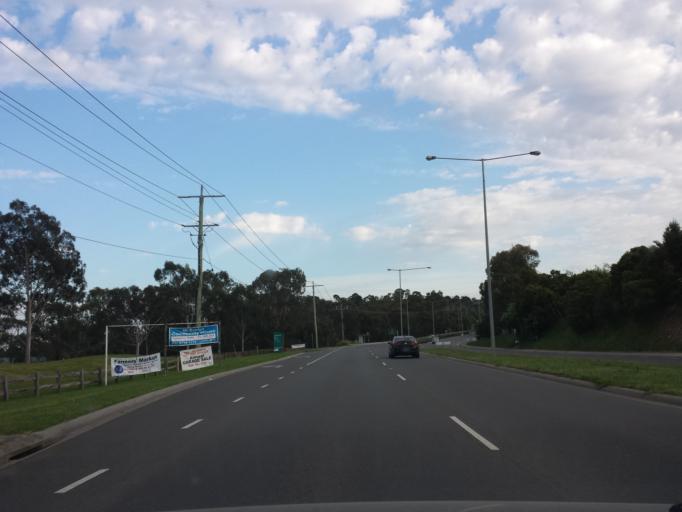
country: AU
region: Victoria
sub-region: Yarra Ranges
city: Lilydale
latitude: -37.7670
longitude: 145.3598
